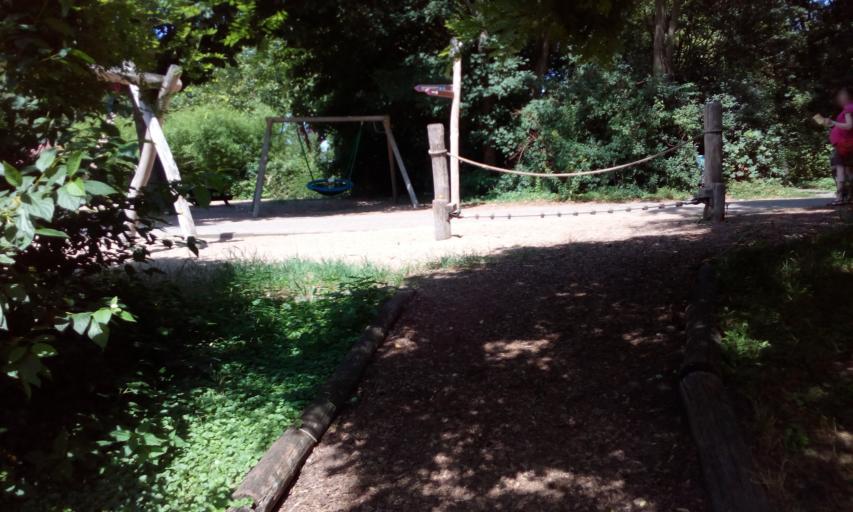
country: NL
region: South Holland
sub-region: Gemeente Alphen aan den Rijn
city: Alphen aan den Rijn
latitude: 52.1397
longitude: 4.6480
